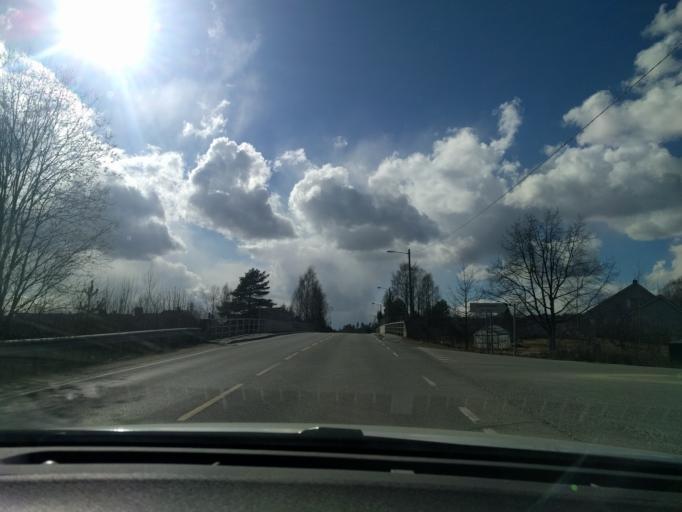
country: NO
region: Hedmark
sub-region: Ringsaker
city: Brumunddal
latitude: 60.8875
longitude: 10.9226
